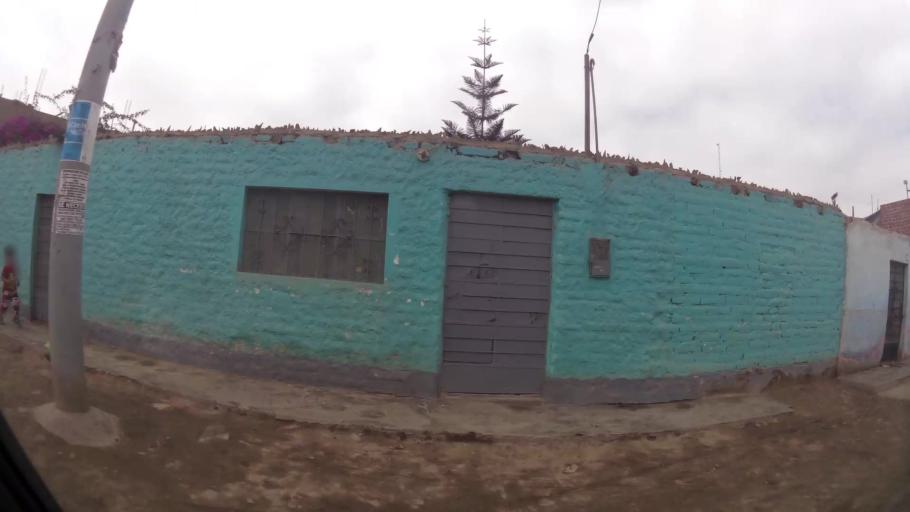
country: PE
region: Lima
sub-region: Provincia de Huaral
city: Huaral
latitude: -11.4896
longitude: -77.2104
